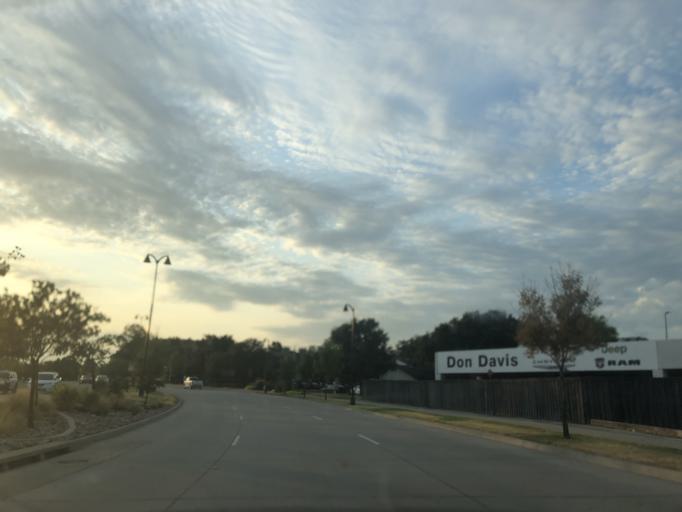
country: US
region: Texas
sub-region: Tarrant County
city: Arlington
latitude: 32.7650
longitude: -97.0952
